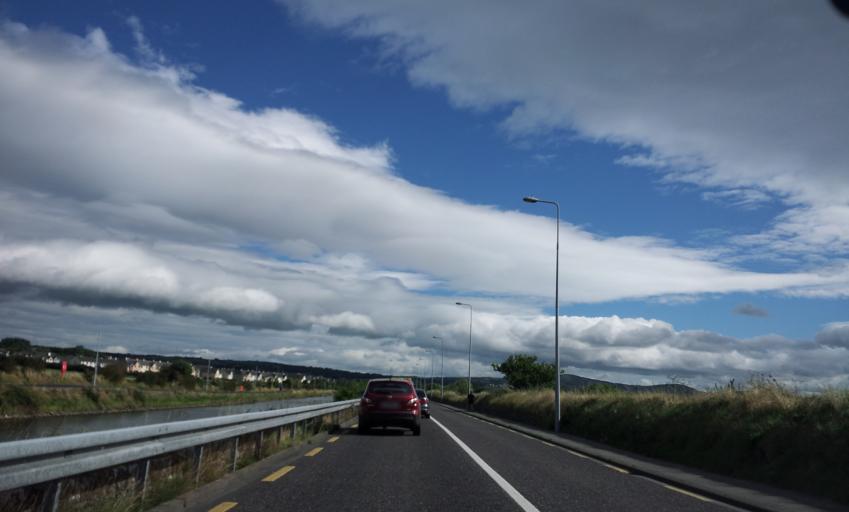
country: IE
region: Munster
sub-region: Ciarrai
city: Tralee
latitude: 52.2601
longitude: -9.7262
